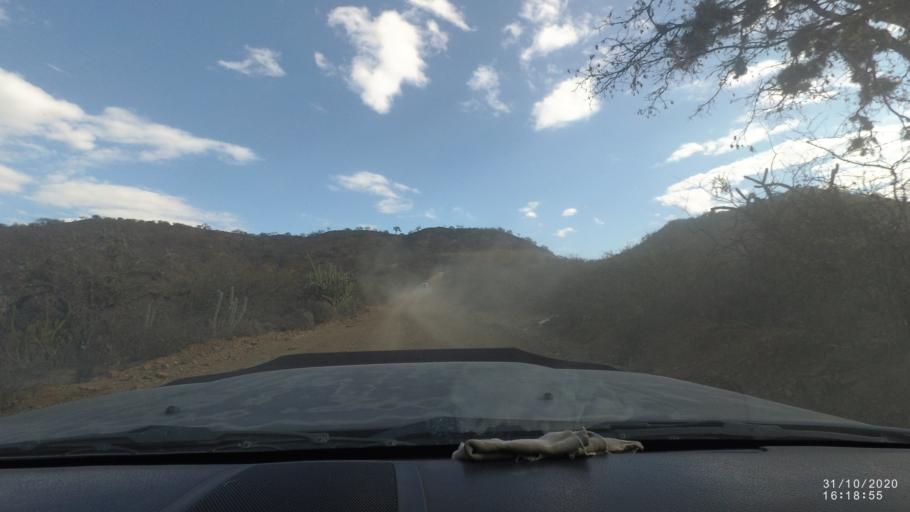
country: BO
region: Chuquisaca
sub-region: Provincia Zudanez
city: Mojocoya
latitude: -18.3931
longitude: -64.6032
